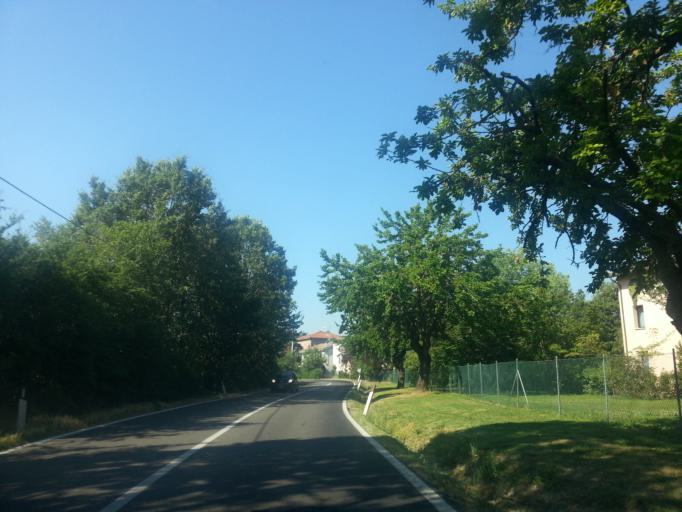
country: IT
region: Emilia-Romagna
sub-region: Provincia di Reggio Emilia
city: Forche
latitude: 44.6424
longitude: 10.5786
